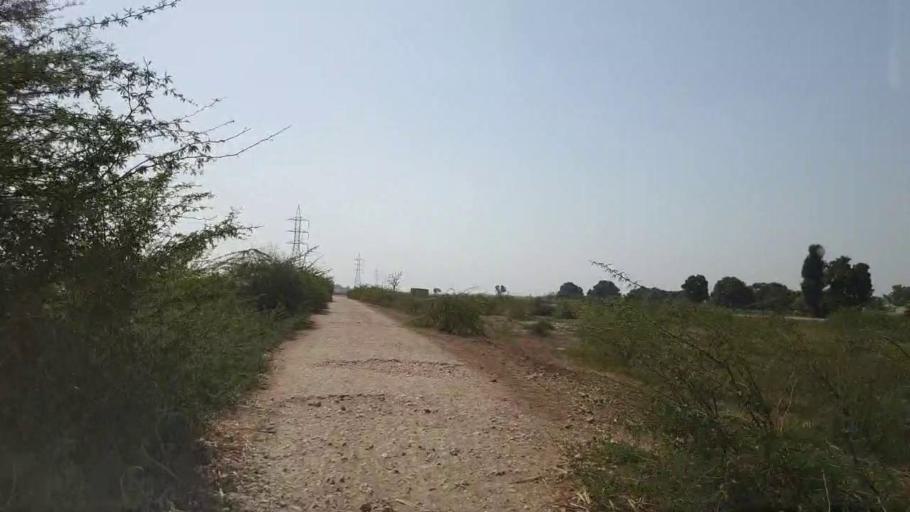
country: PK
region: Sindh
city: Naukot
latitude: 24.9856
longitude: 69.4741
